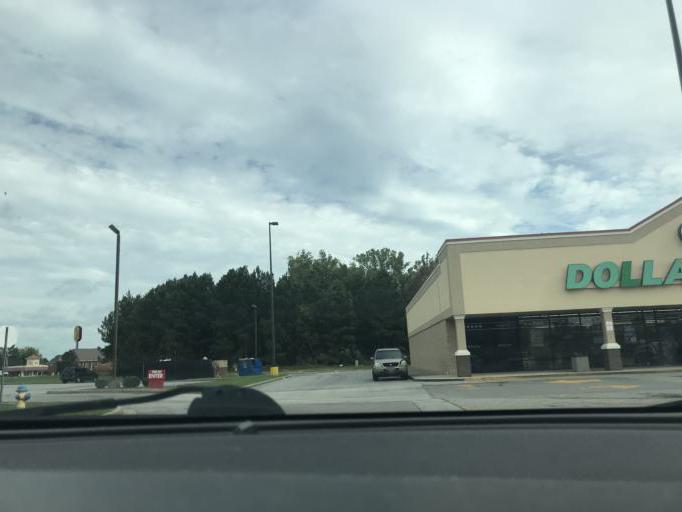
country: US
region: South Carolina
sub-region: Cherokee County
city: Gaffney
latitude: 35.0892
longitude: -81.6626
